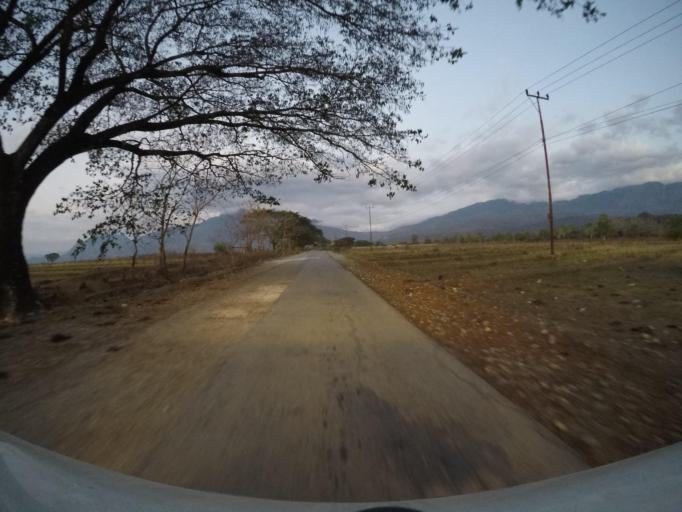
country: TL
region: Bobonaro
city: Maliana
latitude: -8.9911
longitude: 125.1800
